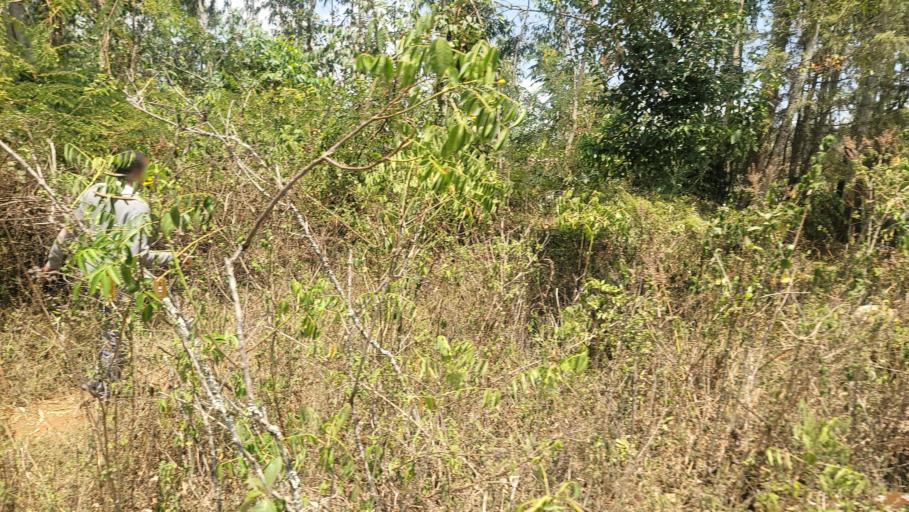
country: ET
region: Oromiya
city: Agaro
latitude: 7.7940
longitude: 36.4852
